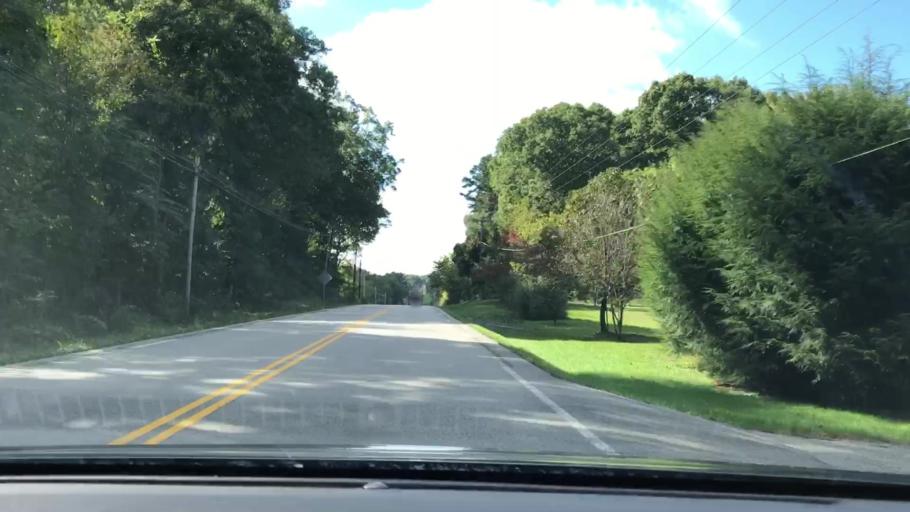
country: US
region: Tennessee
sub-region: Fentress County
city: Jamestown
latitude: 36.3827
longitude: -84.9079
